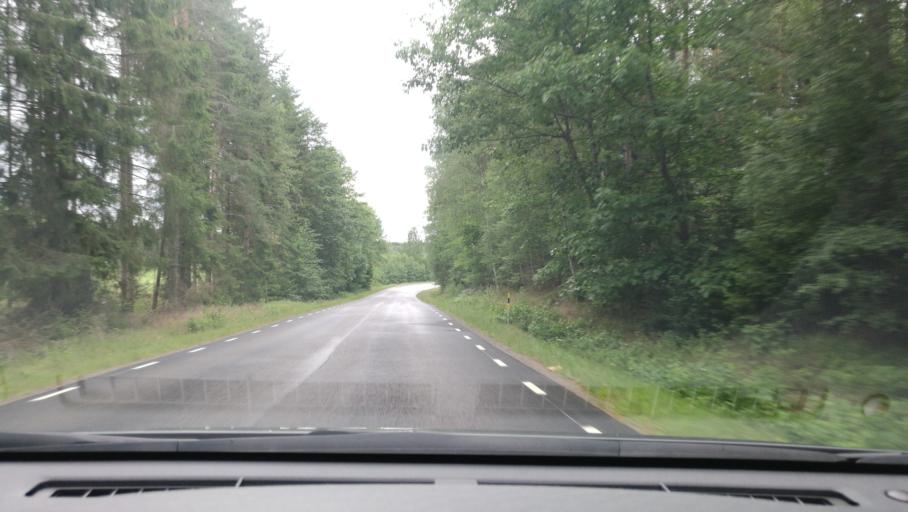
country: SE
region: OEstergoetland
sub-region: Norrkopings Kommun
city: Svartinge
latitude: 58.8194
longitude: 16.0065
